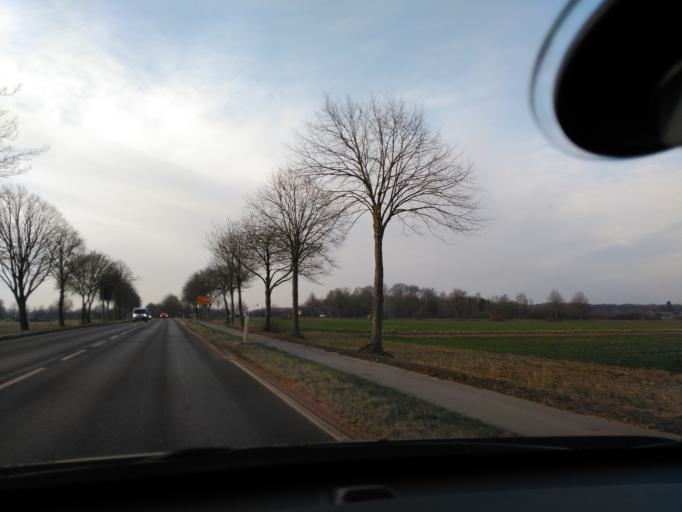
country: DE
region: North Rhine-Westphalia
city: Wegberg
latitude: 51.1419
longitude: 6.3491
